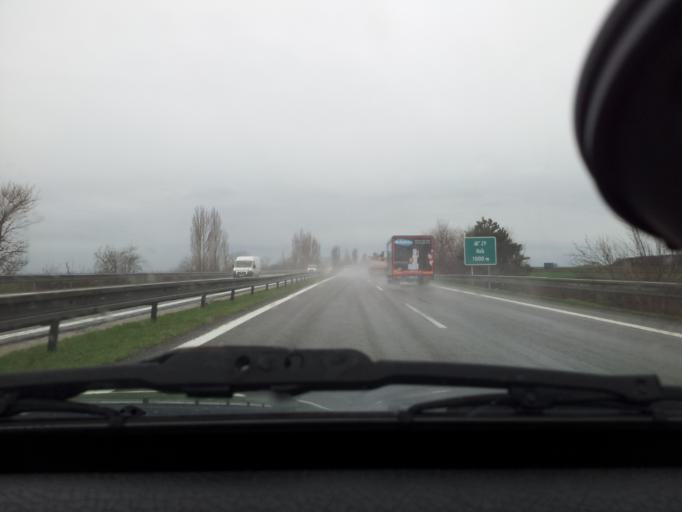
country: SK
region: Nitriansky
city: Sellye
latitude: 48.3023
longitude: 17.9094
